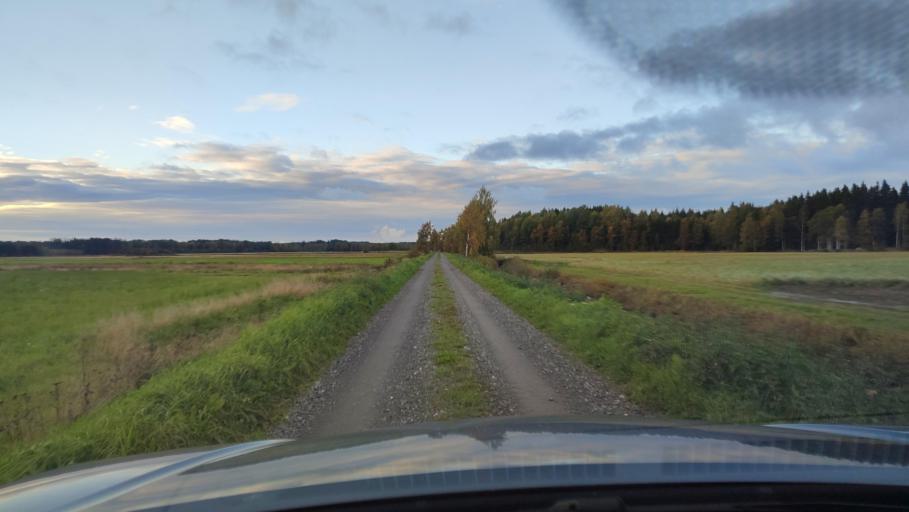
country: FI
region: Ostrobothnia
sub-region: Sydosterbotten
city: Kristinestad
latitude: 62.2419
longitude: 21.4540
